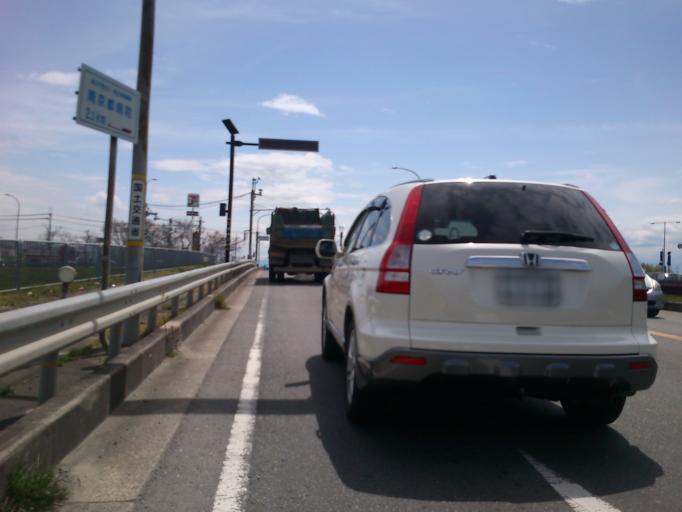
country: JP
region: Kyoto
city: Tanabe
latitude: 34.8233
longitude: 135.7947
